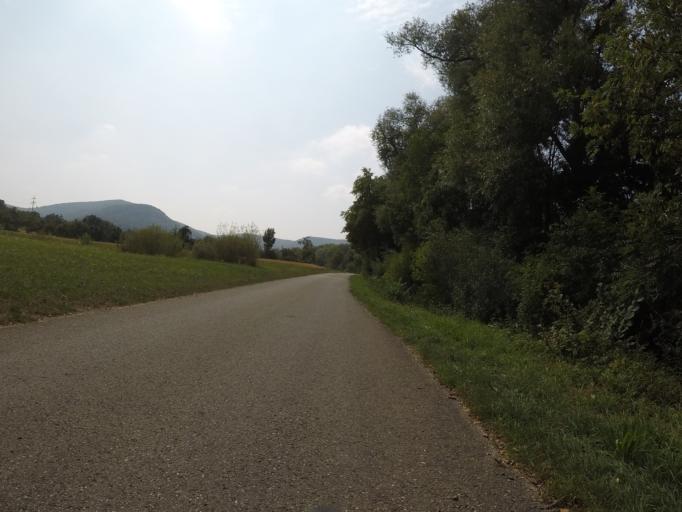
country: DE
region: Baden-Wuerttemberg
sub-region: Tuebingen Region
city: Pfullingen
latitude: 48.4542
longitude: 9.2119
